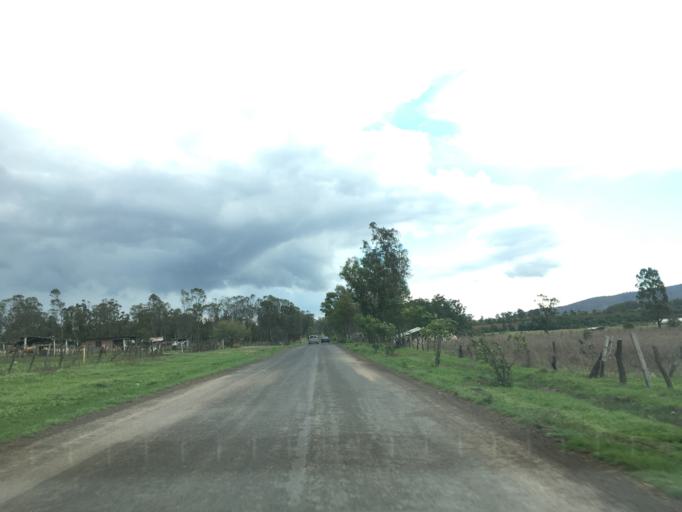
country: MX
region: Michoacan
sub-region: Morelia
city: La Mintzita (Piedra Dura)
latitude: 19.5678
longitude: -101.2743
